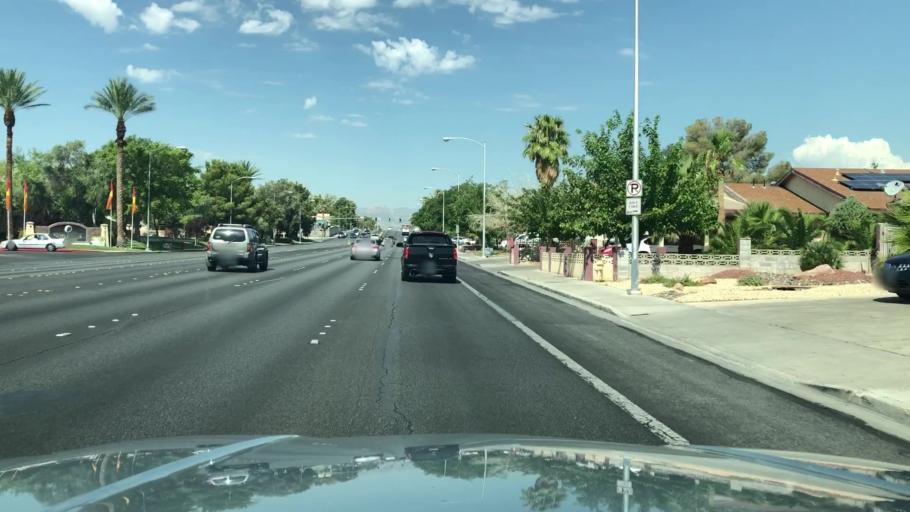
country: US
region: Nevada
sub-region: Clark County
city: Spring Valley
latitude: 36.1298
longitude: -115.2138
